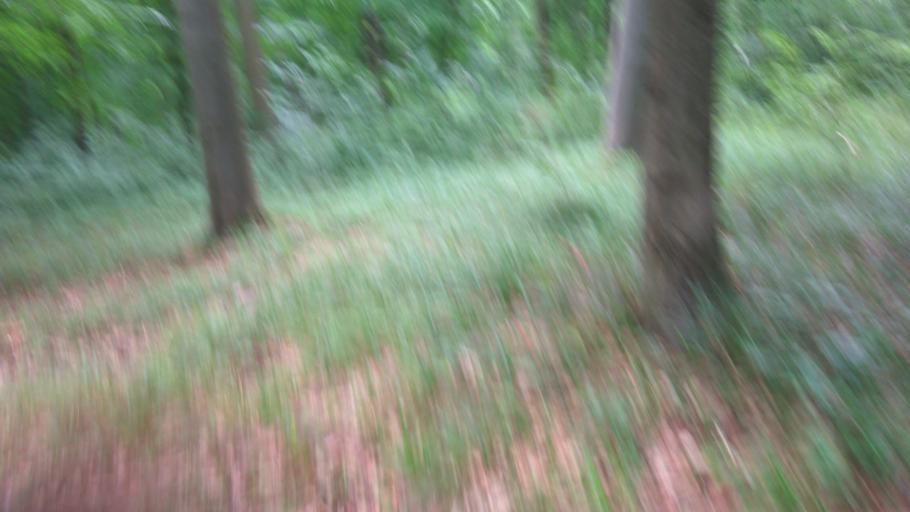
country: HU
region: Komarom-Esztergom
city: Pilismarot
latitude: 47.7342
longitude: 18.8632
